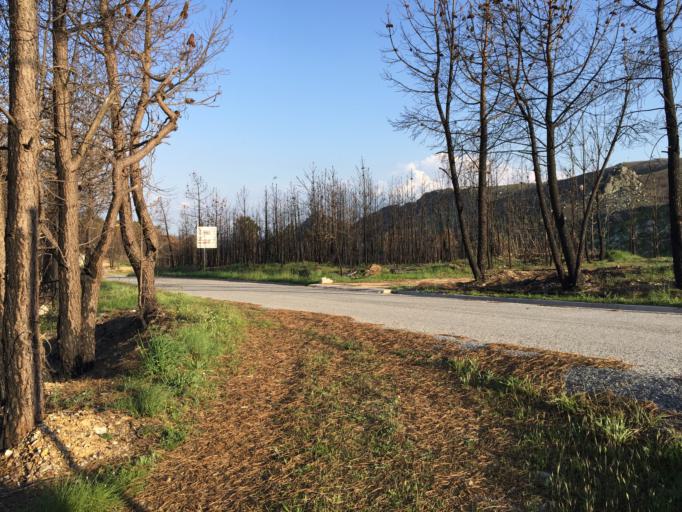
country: PT
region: Coimbra
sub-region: Pampilhosa da Serra
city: Pampilhosa da Serra
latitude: 40.1095
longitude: -7.8729
